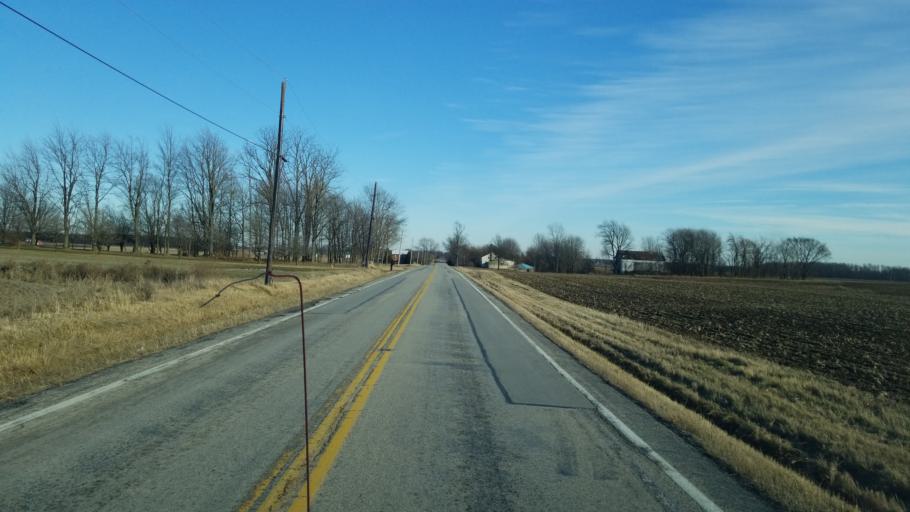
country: US
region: Ohio
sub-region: Huron County
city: Bellevue
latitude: 41.2024
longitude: -82.8337
